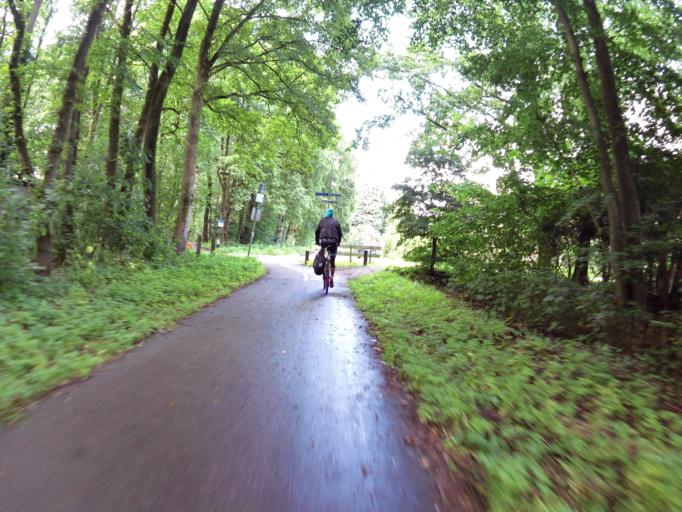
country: NL
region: Utrecht
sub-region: Gemeente Soest
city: Soest
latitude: 52.1616
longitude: 5.2745
